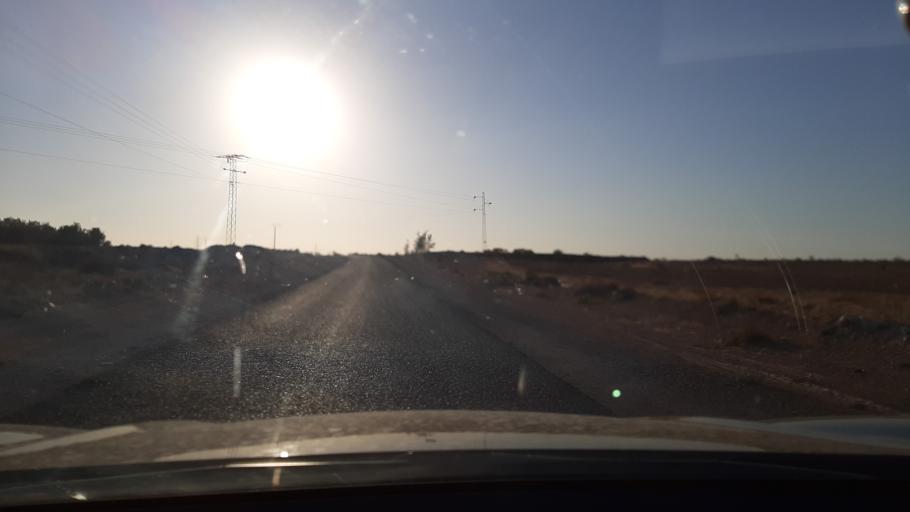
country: TN
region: Qabis
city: Matmata
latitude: 33.6169
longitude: 10.2409
